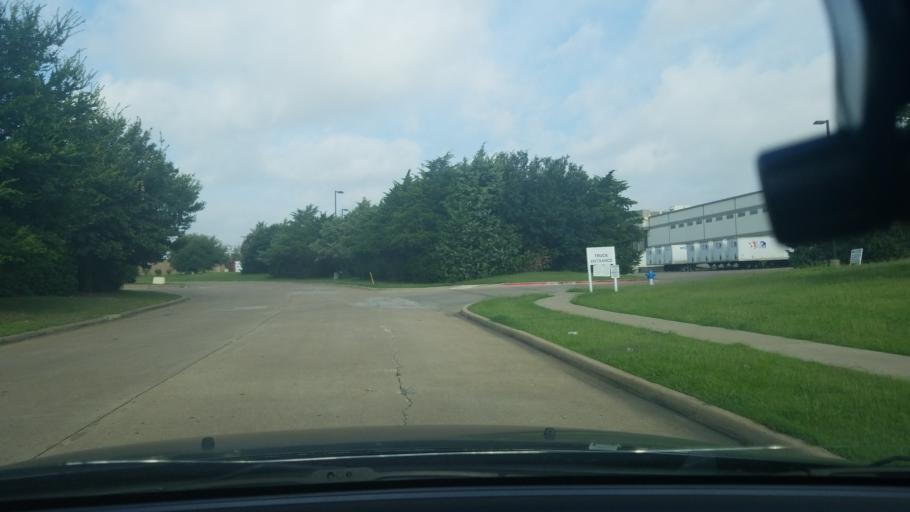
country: US
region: Texas
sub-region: Dallas County
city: Mesquite
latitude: 32.7749
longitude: -96.6501
